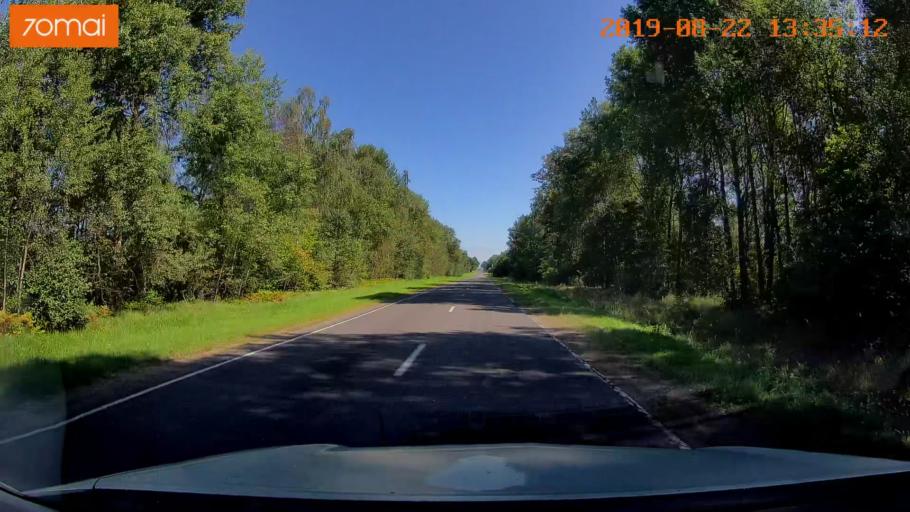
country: BY
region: Minsk
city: Staryya Darohi
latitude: 53.2140
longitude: 28.2621
